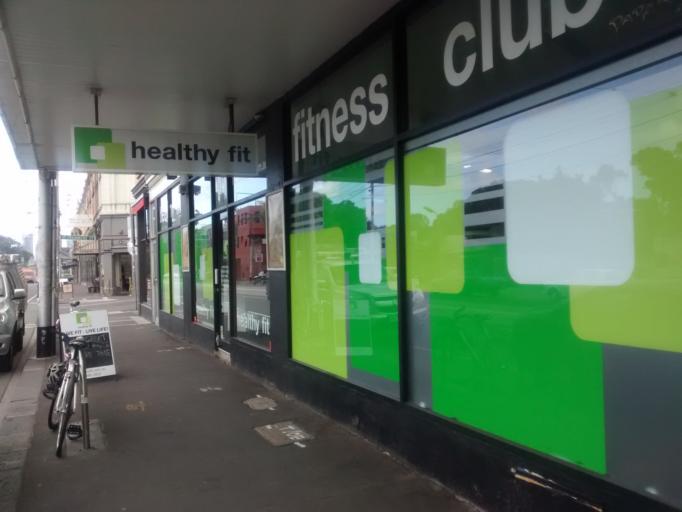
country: AU
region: Victoria
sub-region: Yarra
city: North Fitzroy
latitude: -37.7845
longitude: 144.9827
